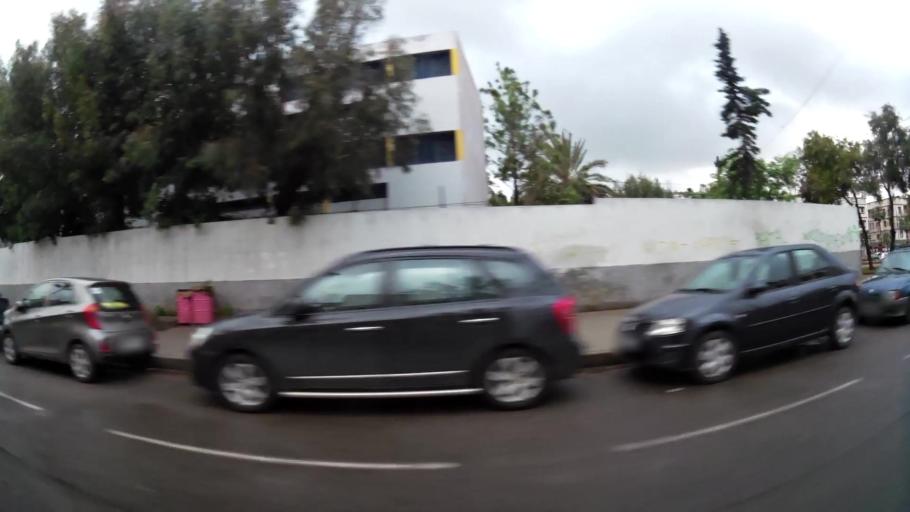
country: MA
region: Grand Casablanca
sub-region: Casablanca
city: Casablanca
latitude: 33.5626
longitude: -7.6054
